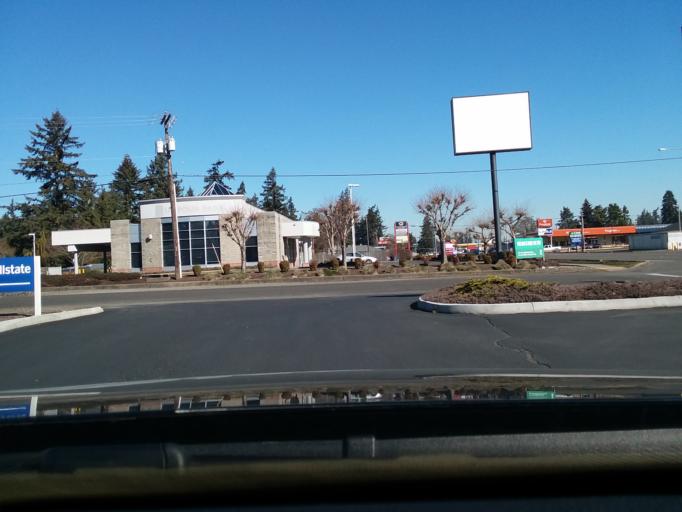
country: US
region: Washington
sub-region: Pierce County
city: Spanaway
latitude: 47.1093
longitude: -122.4351
